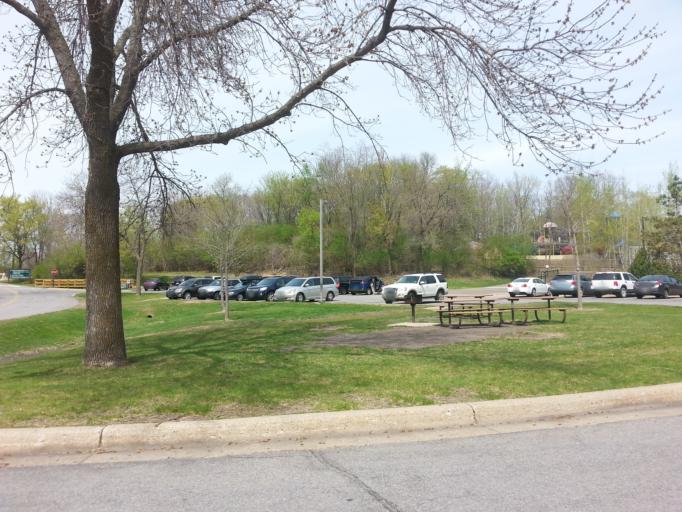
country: US
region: Minnesota
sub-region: Scott County
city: Savage
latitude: 44.8246
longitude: -93.3723
